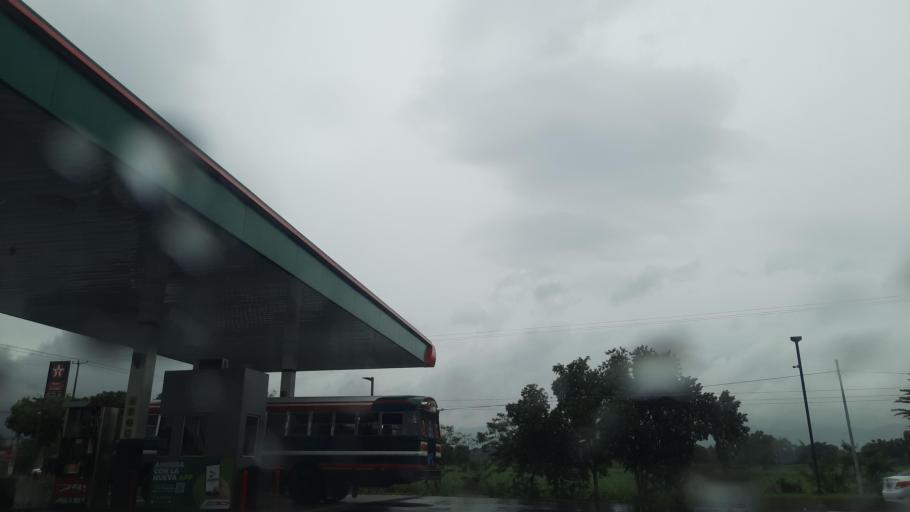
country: SV
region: La Libertad
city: Ciudad Arce
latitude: 13.7658
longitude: -89.3705
